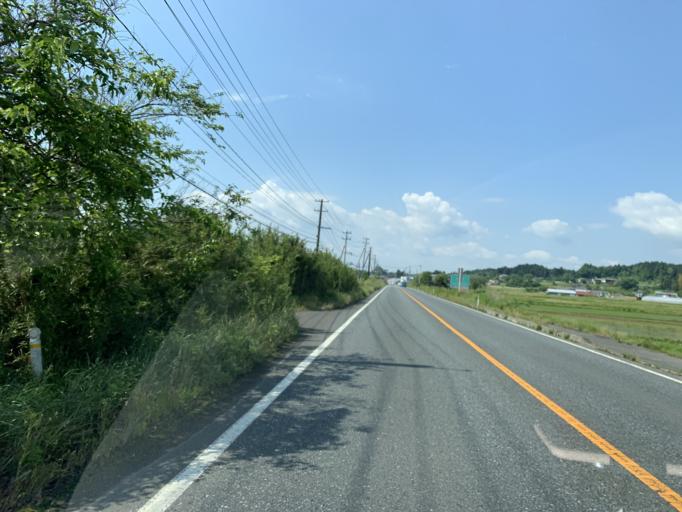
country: JP
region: Iwate
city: Ichinoseki
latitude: 38.8206
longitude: 141.0781
